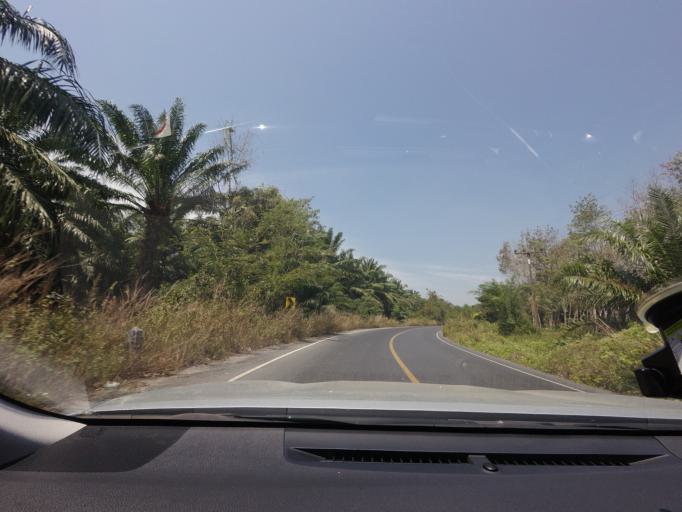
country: TH
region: Surat Thani
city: Tha Chang
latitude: 9.2635
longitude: 99.1636
